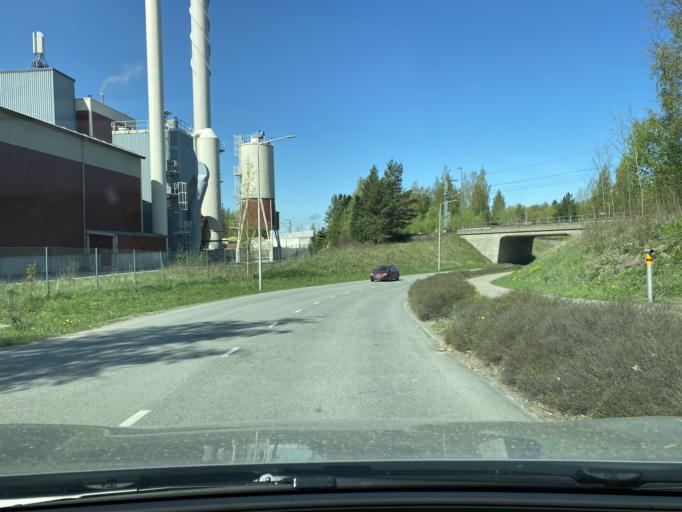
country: FI
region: Pirkanmaa
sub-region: Lounais-Pirkanmaa
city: Vammala
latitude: 61.3489
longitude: 22.8839
